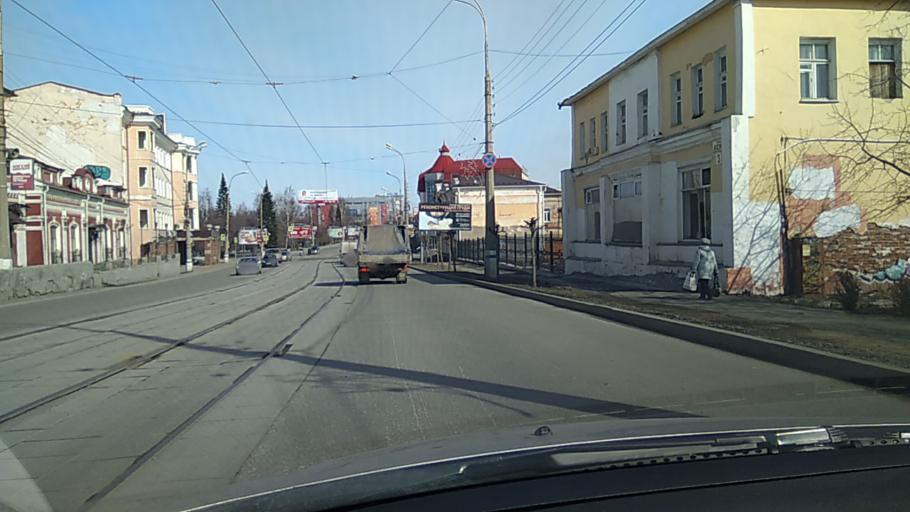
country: RU
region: Sverdlovsk
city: Nizhniy Tagil
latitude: 57.9064
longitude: 59.9535
